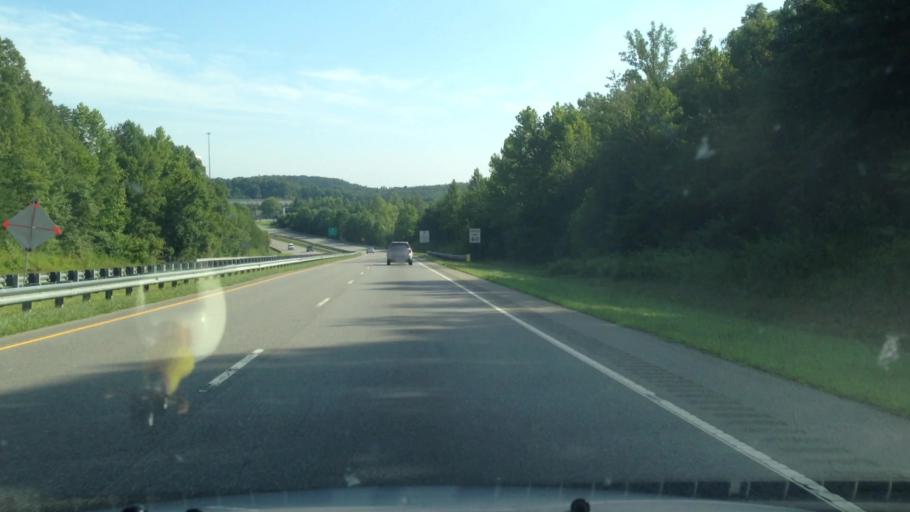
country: US
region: North Carolina
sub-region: Rockingham County
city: Stoneville
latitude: 36.4545
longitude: -79.9277
